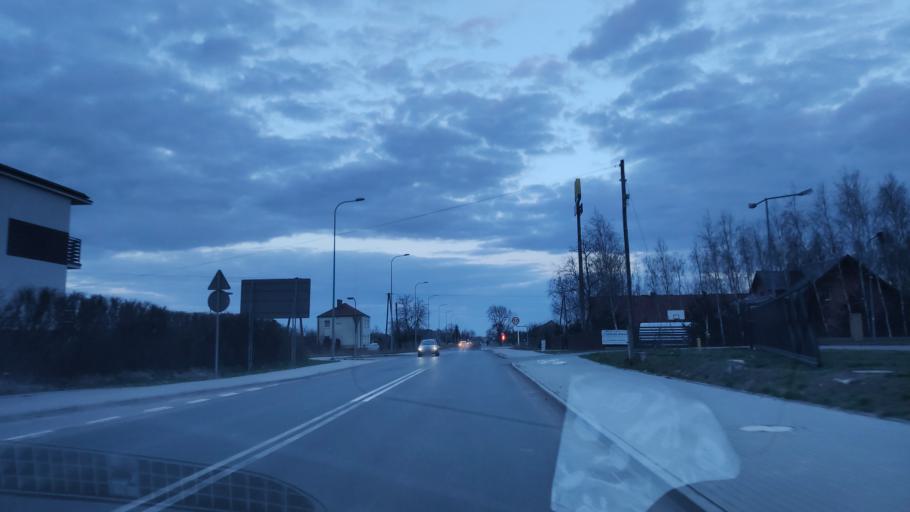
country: PL
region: Kujawsko-Pomorskie
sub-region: Powiat zninski
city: Znin
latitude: 52.8498
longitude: 17.6956
